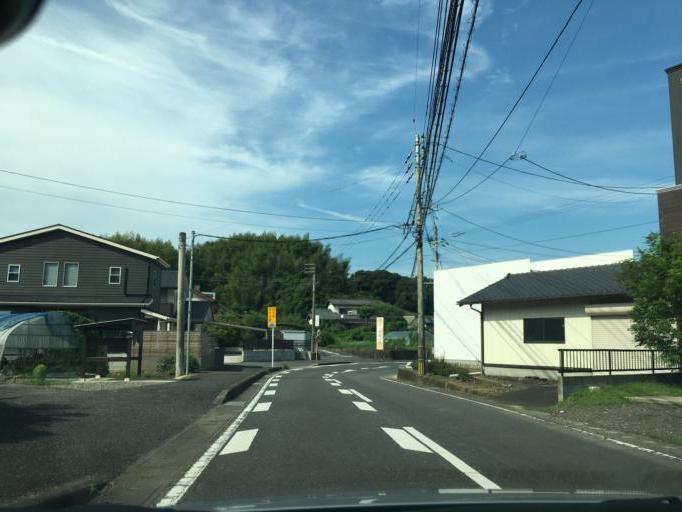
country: JP
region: Saga Prefecture
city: Takeocho-takeo
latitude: 33.1888
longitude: 130.0326
